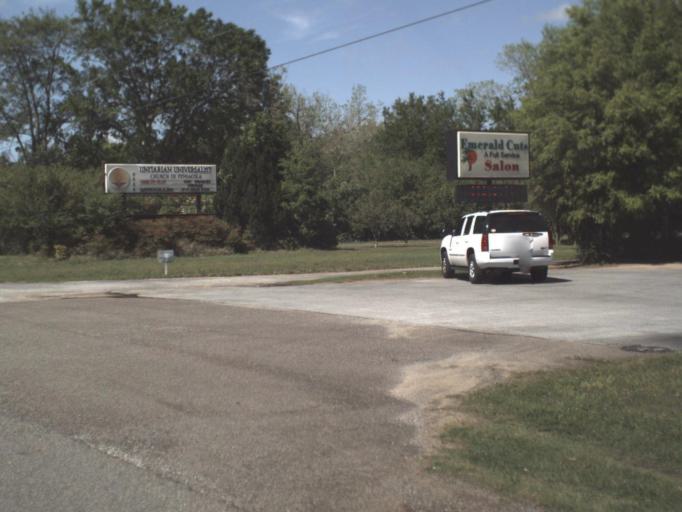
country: US
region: Florida
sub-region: Escambia County
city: Ensley
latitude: 30.5390
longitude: -87.2798
